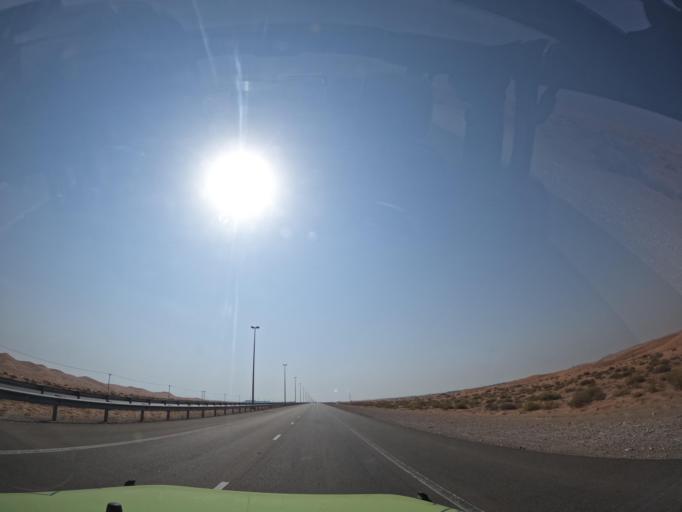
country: OM
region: Al Buraimi
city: Al Buraymi
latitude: 24.4288
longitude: 55.6797
